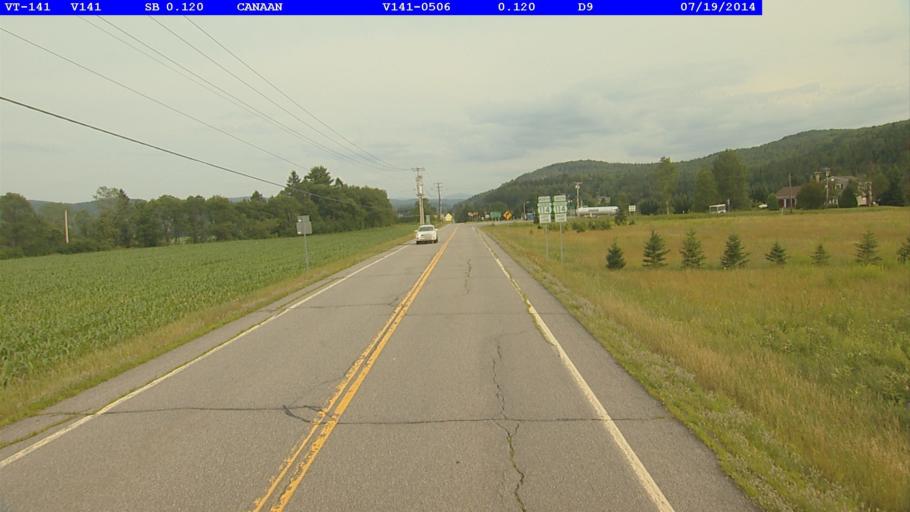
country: US
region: New Hampshire
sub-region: Coos County
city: Colebrook
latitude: 45.0084
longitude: -71.5569
